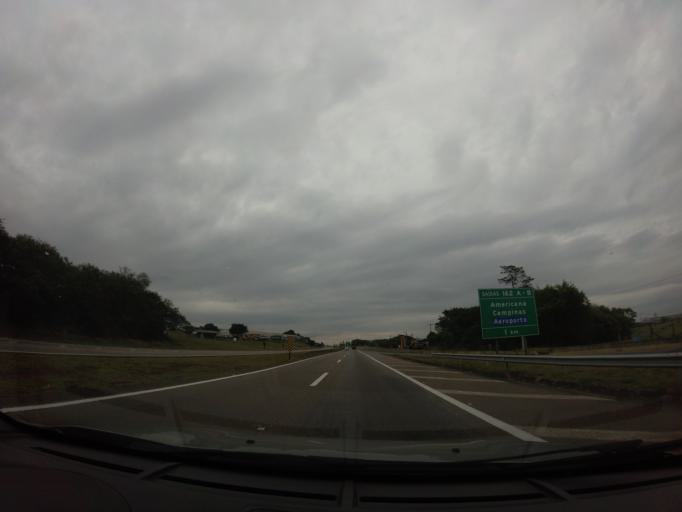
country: BR
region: Sao Paulo
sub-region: Piracicaba
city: Piracicaba
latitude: -22.7336
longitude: -47.6023
